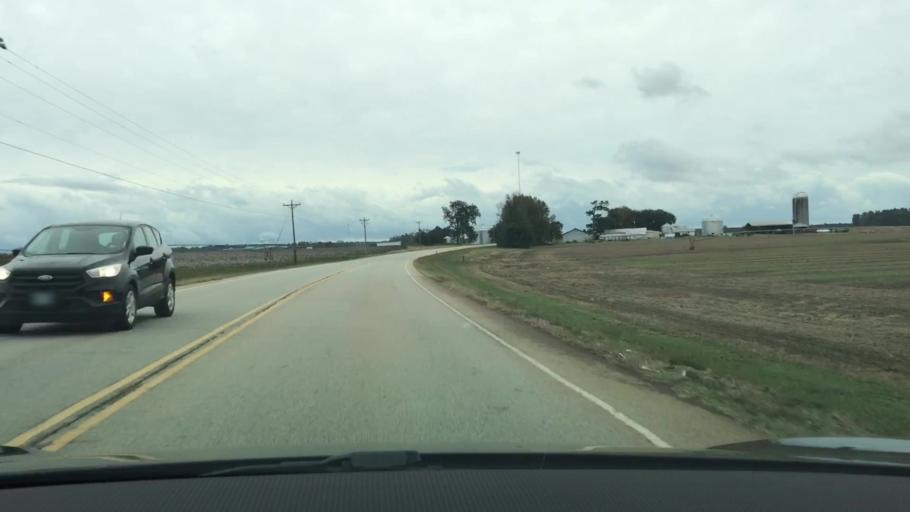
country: US
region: Georgia
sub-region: Jefferson County
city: Wrens
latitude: 33.1120
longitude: -82.4296
